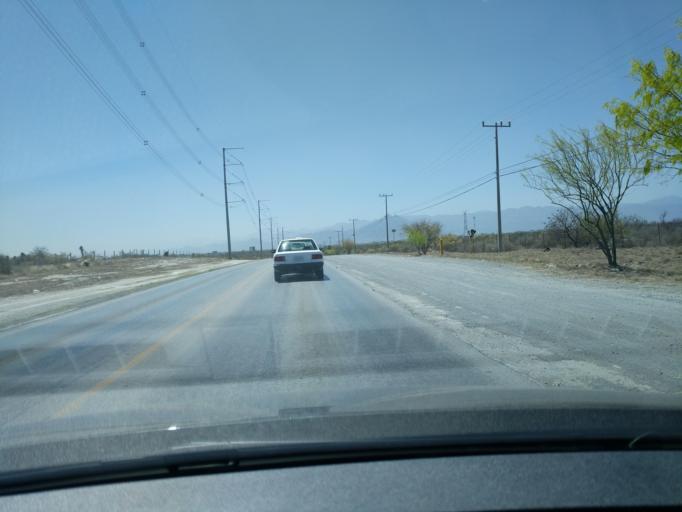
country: MX
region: Nuevo Leon
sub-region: Apodaca
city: Artemio Trevino
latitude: 25.8257
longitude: -100.1438
